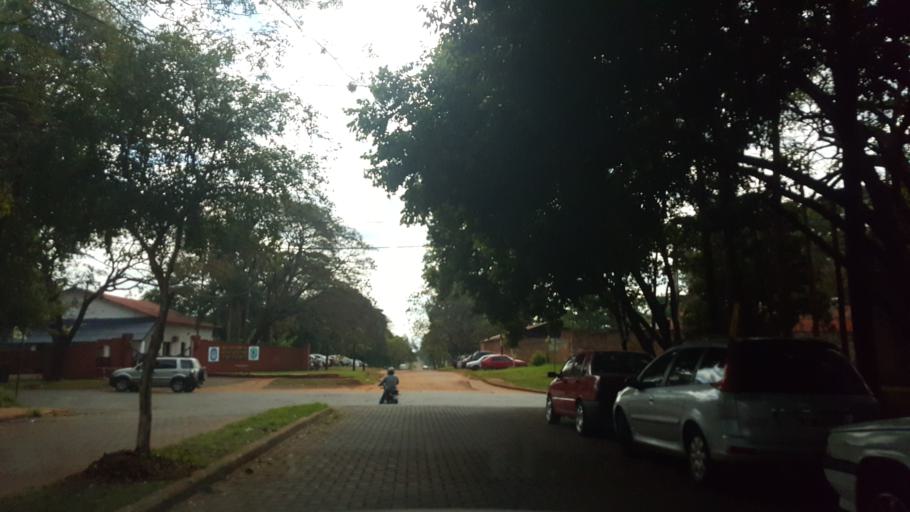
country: AR
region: Misiones
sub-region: Departamento de Capital
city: Posadas
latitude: -27.3655
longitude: -55.9201
